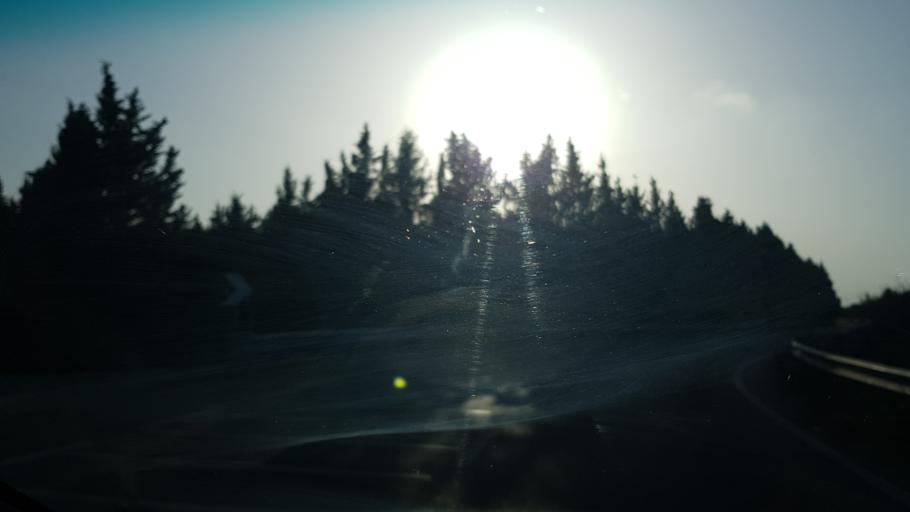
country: IT
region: Apulia
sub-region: Provincia di Lecce
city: Trepuzzi
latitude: 40.3986
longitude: 18.0566
